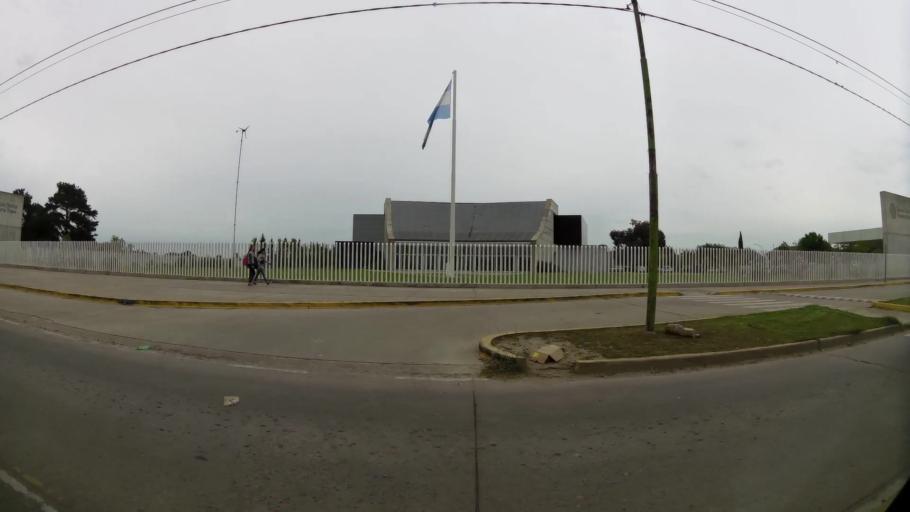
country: AR
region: Buenos Aires
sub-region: Partido de Campana
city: Campana
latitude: -34.2007
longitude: -58.9375
